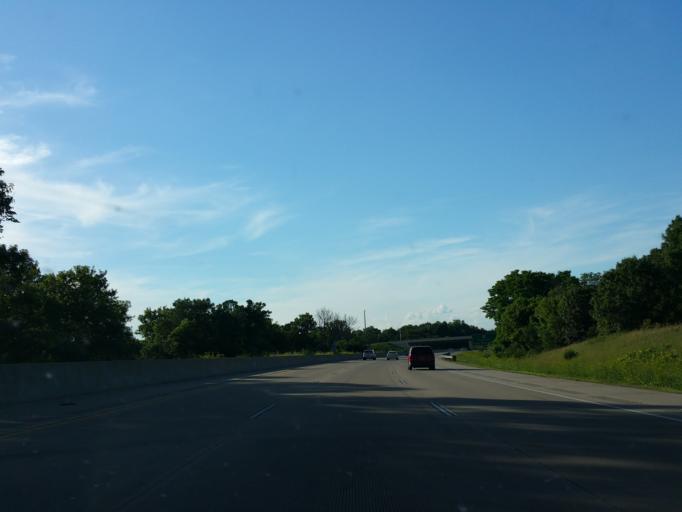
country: US
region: Wisconsin
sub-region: Columbia County
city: Poynette
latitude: 43.3882
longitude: -89.4655
